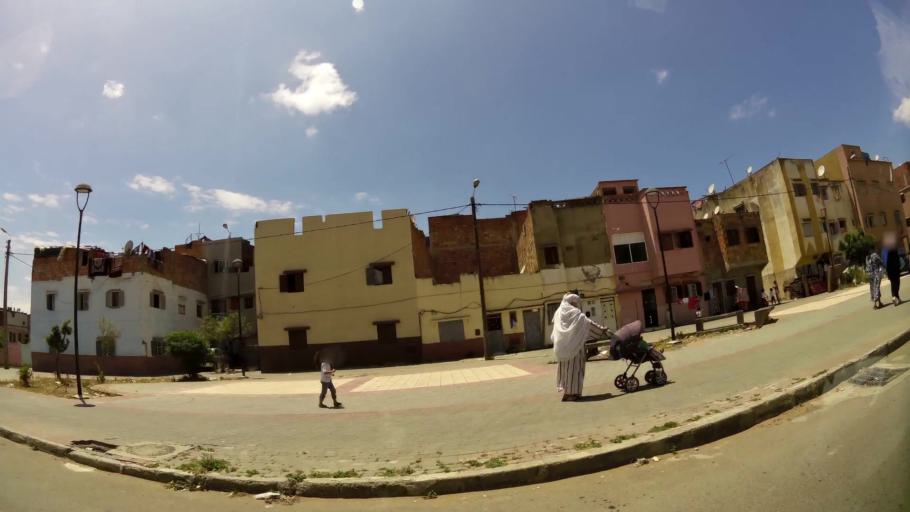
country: MA
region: Gharb-Chrarda-Beni Hssen
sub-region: Kenitra Province
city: Kenitra
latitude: 34.2617
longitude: -6.5564
